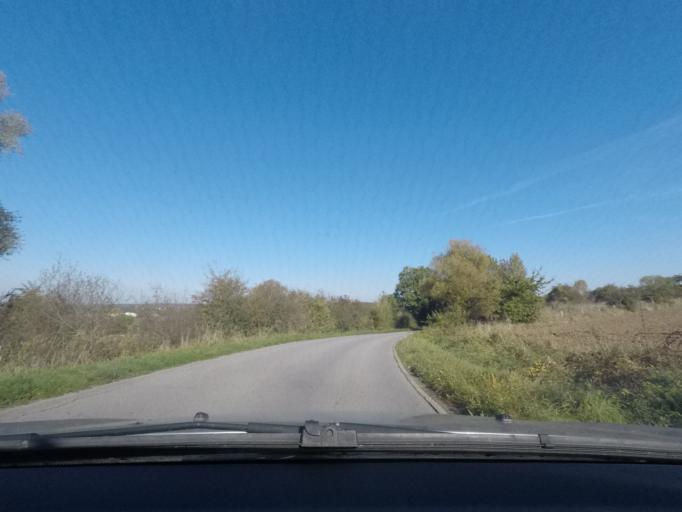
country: BE
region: Wallonia
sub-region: Province du Luxembourg
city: Etalle
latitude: 49.7096
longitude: 5.5657
